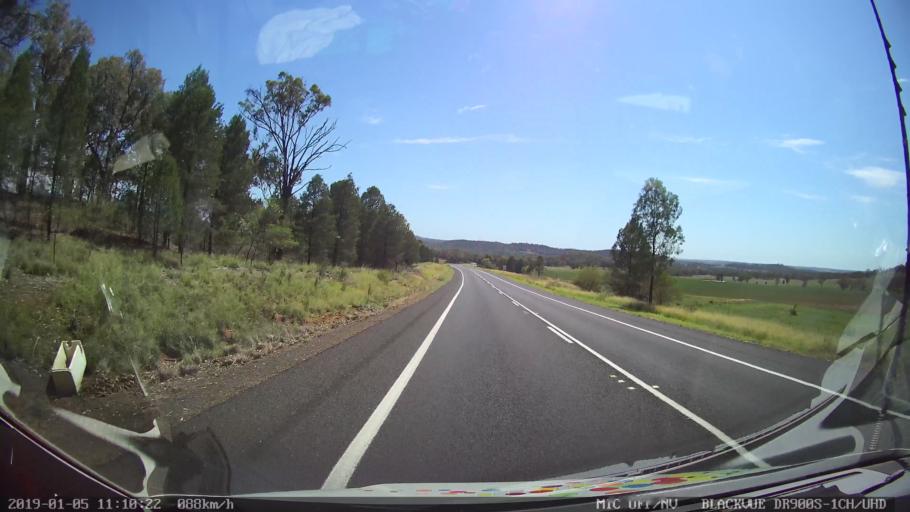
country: AU
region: New South Wales
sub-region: Warrumbungle Shire
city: Coonabarabran
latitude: -31.4073
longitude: 149.2436
